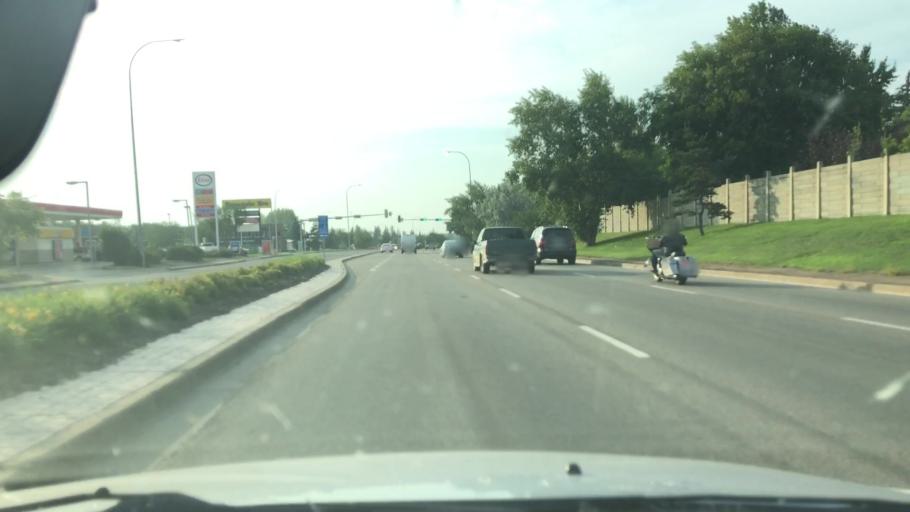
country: CA
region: Alberta
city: St. Albert
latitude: 53.6264
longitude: -113.6170
